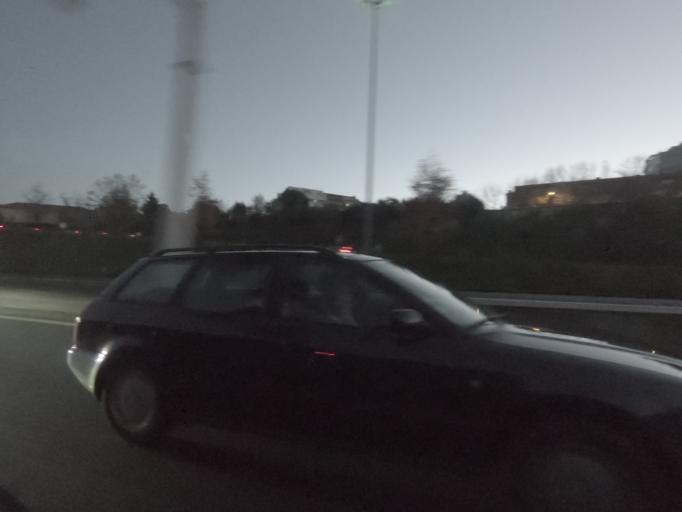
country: PT
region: Porto
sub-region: Porto
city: Porto
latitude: 41.1723
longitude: -8.6066
